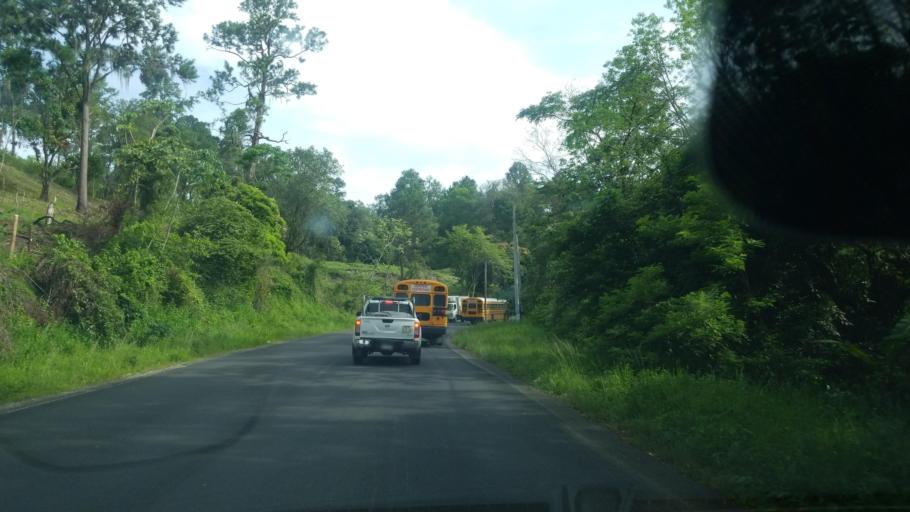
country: HN
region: Santa Barbara
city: Trinidad
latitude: 15.1938
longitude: -88.2731
